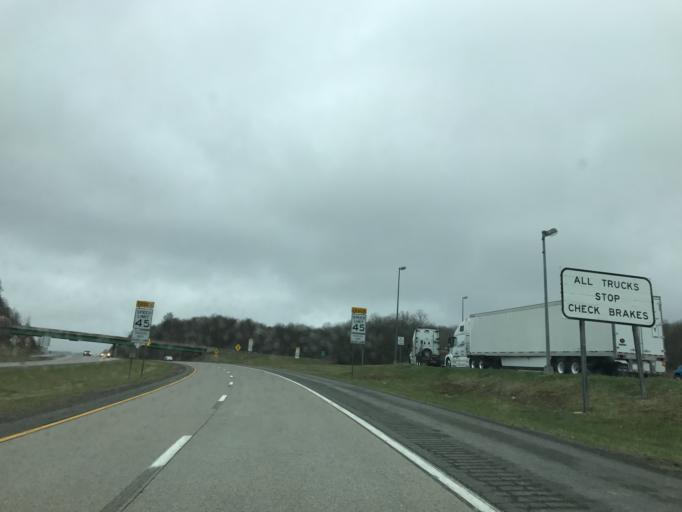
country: US
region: West Virginia
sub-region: Raleigh County
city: Shady Spring
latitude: 37.7675
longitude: -80.9874
